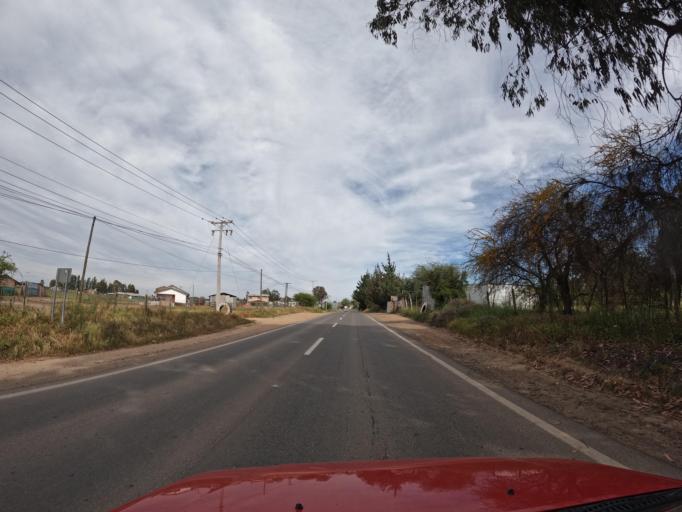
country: CL
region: Maule
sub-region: Provincia de Talca
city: Talca
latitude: -35.3903
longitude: -71.8136
